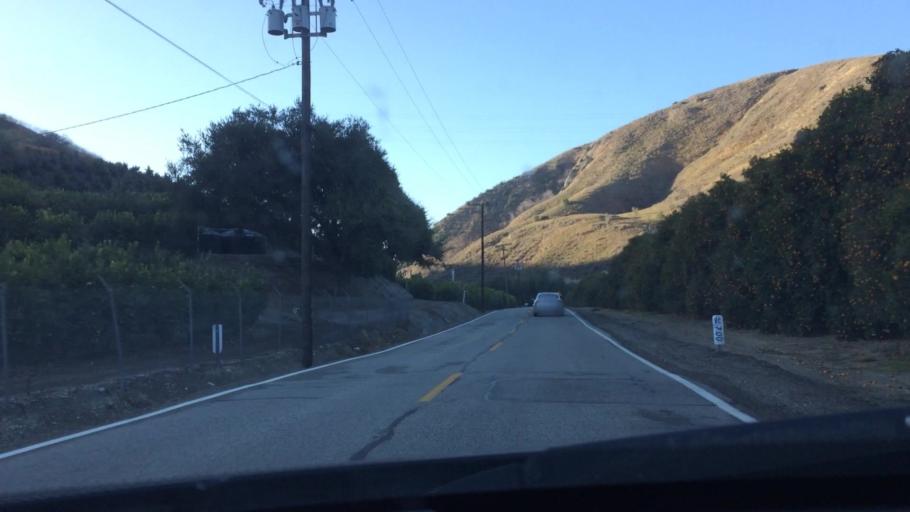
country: US
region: California
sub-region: Ventura County
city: Santa Paula
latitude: 34.3504
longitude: -118.9809
